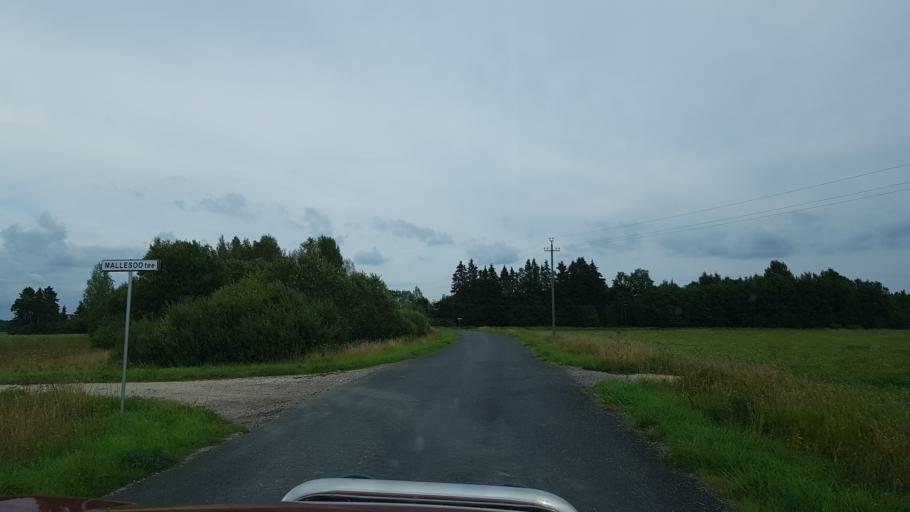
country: EE
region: Laeaene
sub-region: Ridala Parish
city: Uuemoisa
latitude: 58.9828
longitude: 23.7954
